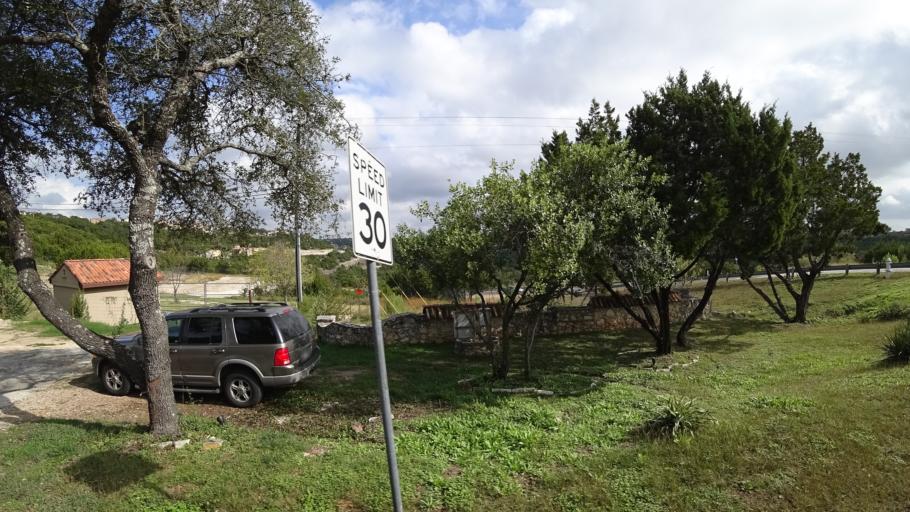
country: US
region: Texas
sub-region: Travis County
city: Hudson Bend
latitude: 30.4083
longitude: -97.8746
